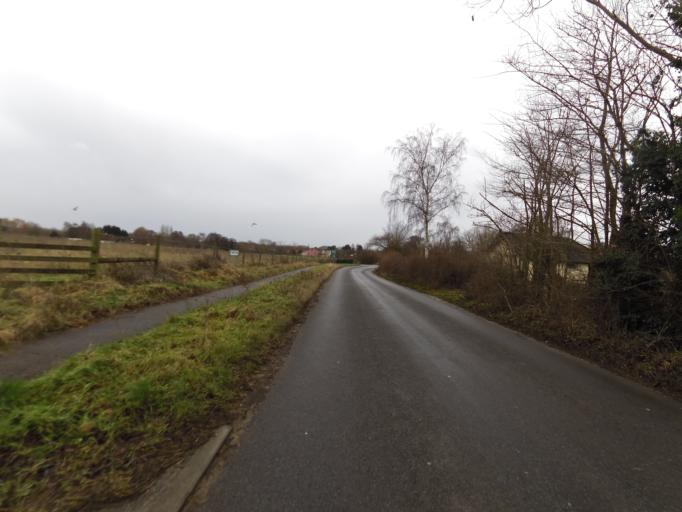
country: GB
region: England
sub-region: Suffolk
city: Needham Market
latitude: 52.1582
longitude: 1.0542
